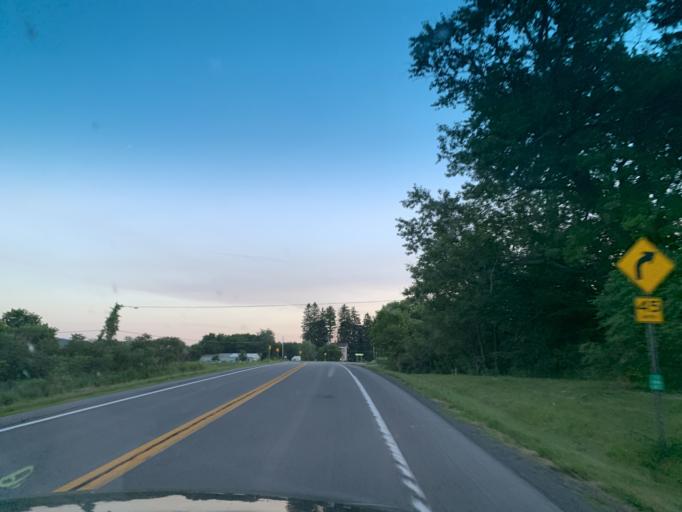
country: US
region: New York
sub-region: Chenango County
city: New Berlin
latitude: 42.7898
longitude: -75.2602
